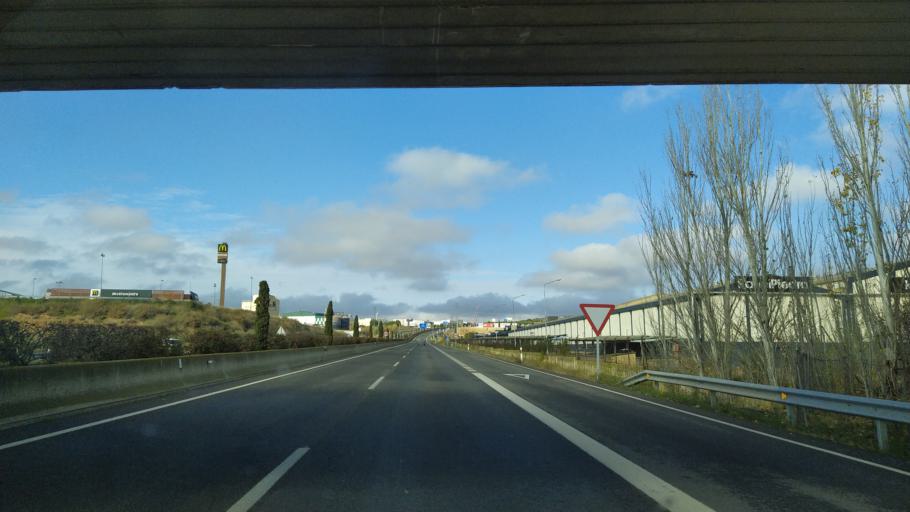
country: ES
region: Navarre
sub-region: Provincia de Navarra
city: Tudela
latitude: 42.0588
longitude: -1.6289
